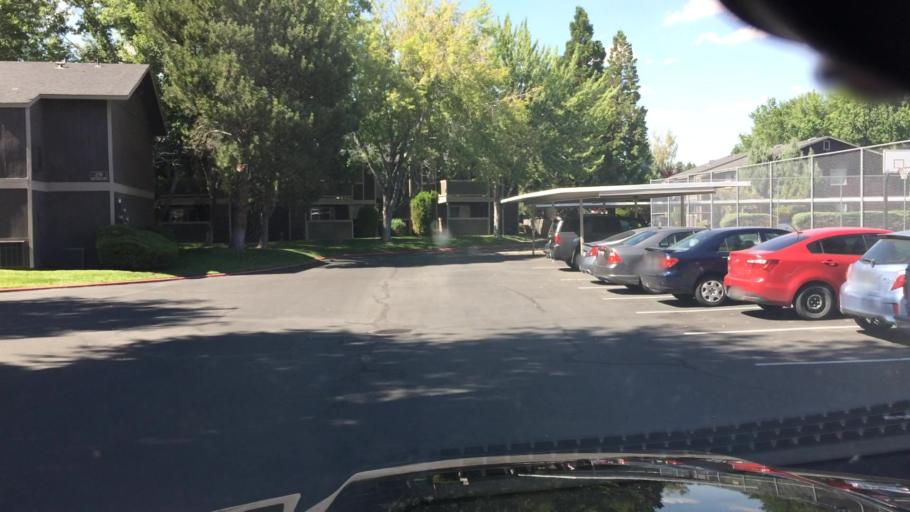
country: US
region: Nevada
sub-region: Washoe County
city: Sparks
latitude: 39.4828
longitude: -119.7461
